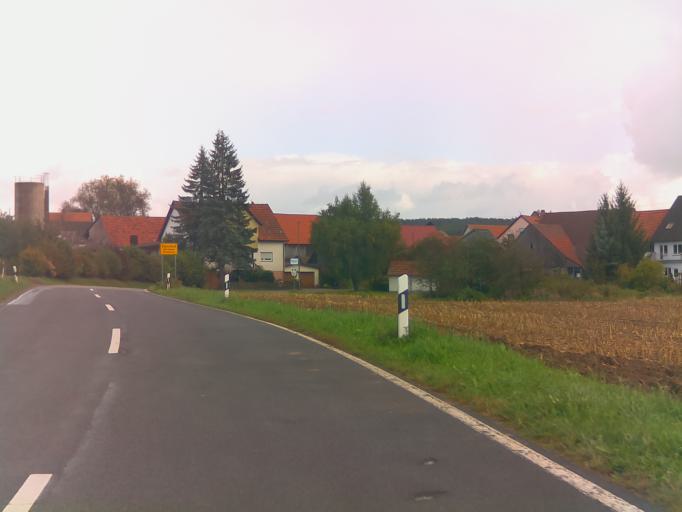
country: DE
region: Baden-Wuerttemberg
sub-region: Karlsruhe Region
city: Hardheim
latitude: 49.6494
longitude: 9.4815
